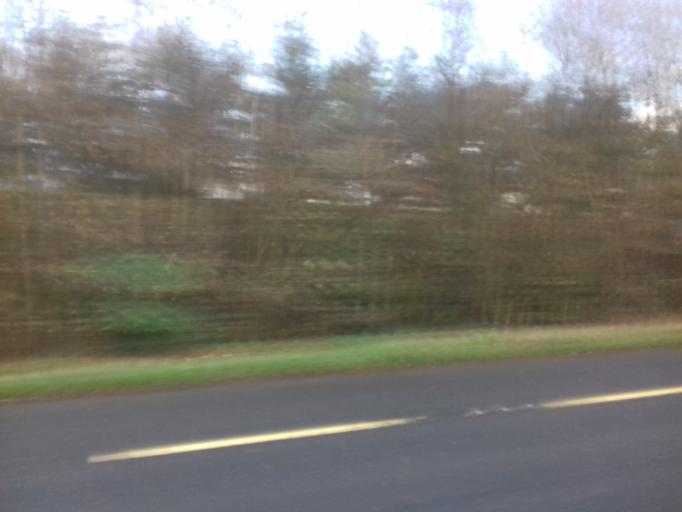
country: IE
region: Leinster
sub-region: Lu
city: Ardee
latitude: 53.8739
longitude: -6.5552
